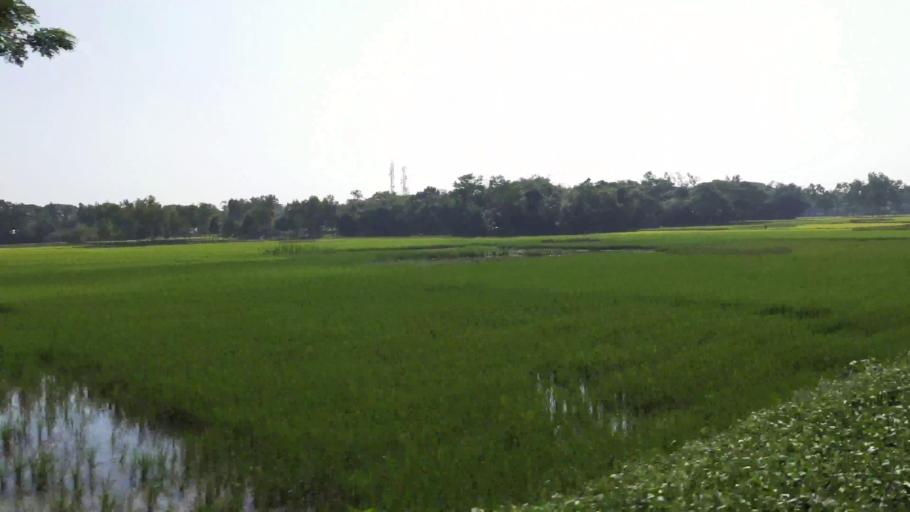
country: BD
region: Dhaka
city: Gafargaon
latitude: 24.5695
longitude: 90.5082
